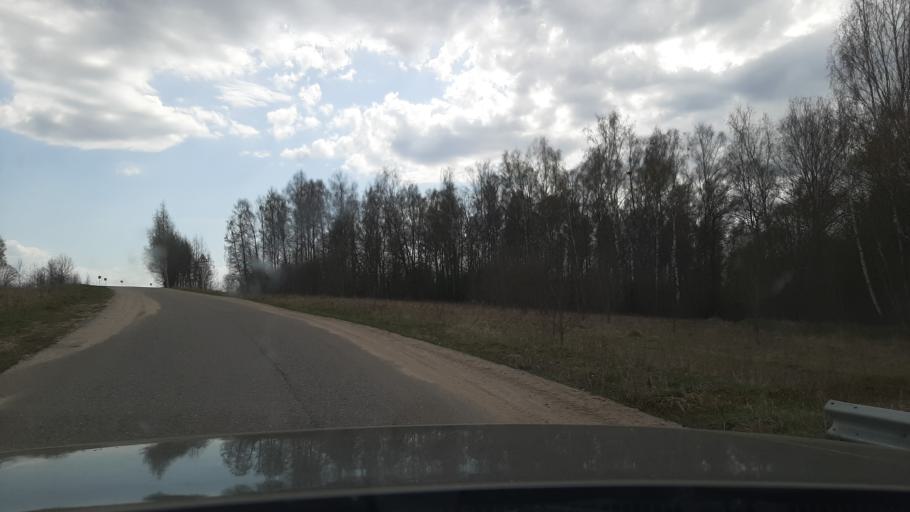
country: RU
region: Ivanovo
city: Furmanov
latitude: 57.3145
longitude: 41.1641
